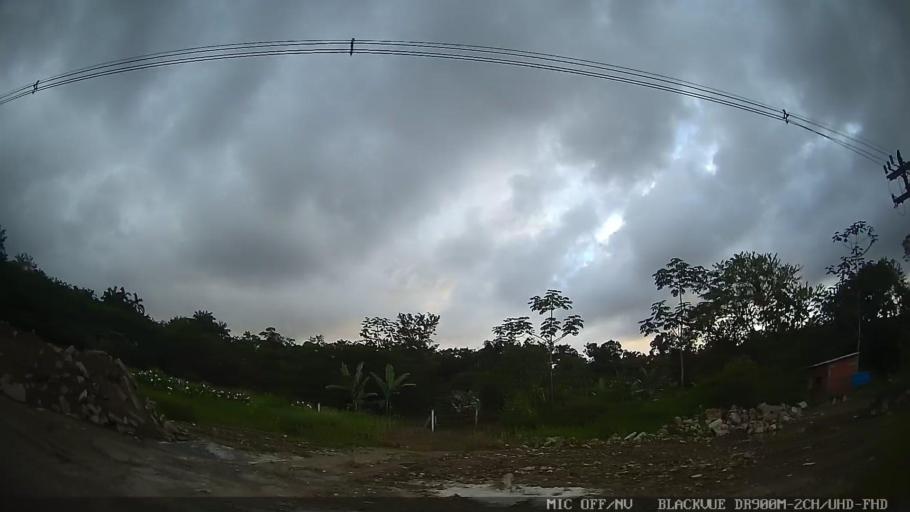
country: BR
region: Sao Paulo
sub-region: Itanhaem
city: Itanhaem
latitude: -24.0870
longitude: -46.7980
